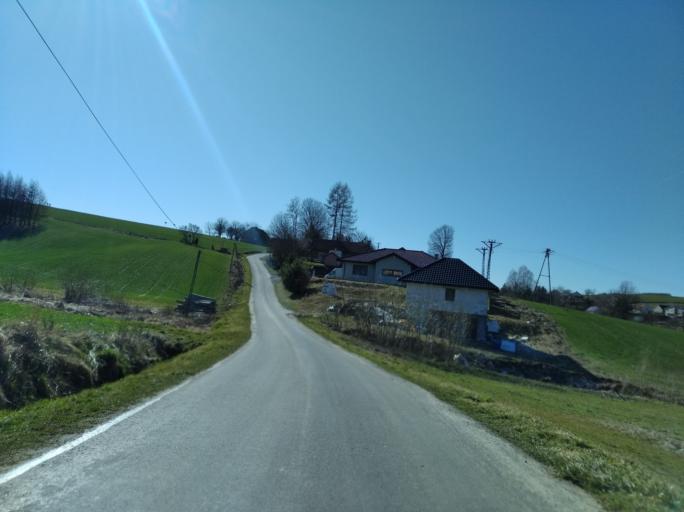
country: PL
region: Subcarpathian Voivodeship
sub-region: Powiat strzyzowski
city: Wisniowa
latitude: 49.9116
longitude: 21.7005
